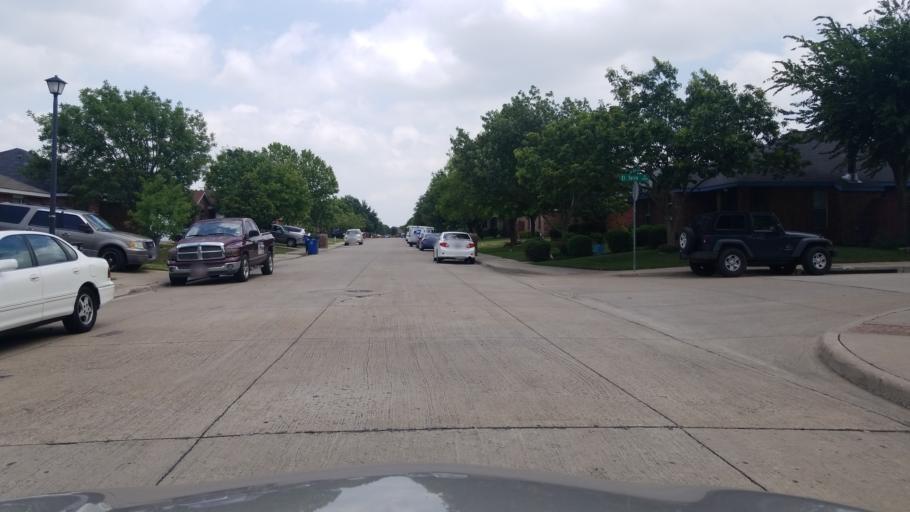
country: US
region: Texas
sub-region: Dallas County
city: Duncanville
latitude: 32.6869
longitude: -96.9178
